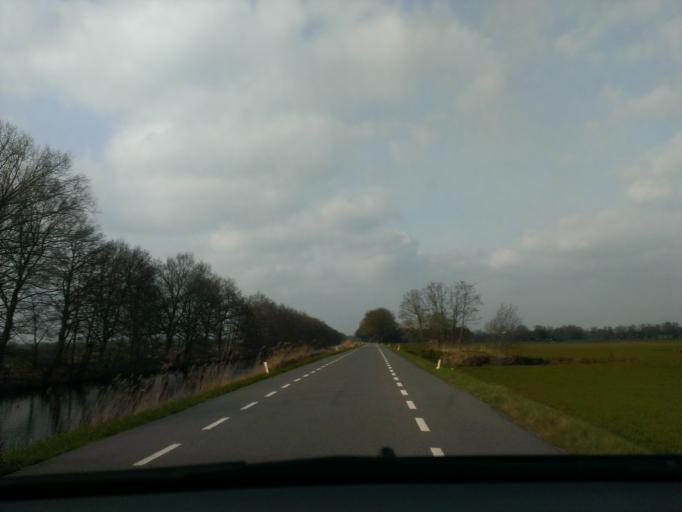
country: NL
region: Gelderland
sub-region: Gemeente Epe
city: Emst
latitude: 52.3205
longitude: 6.0119
